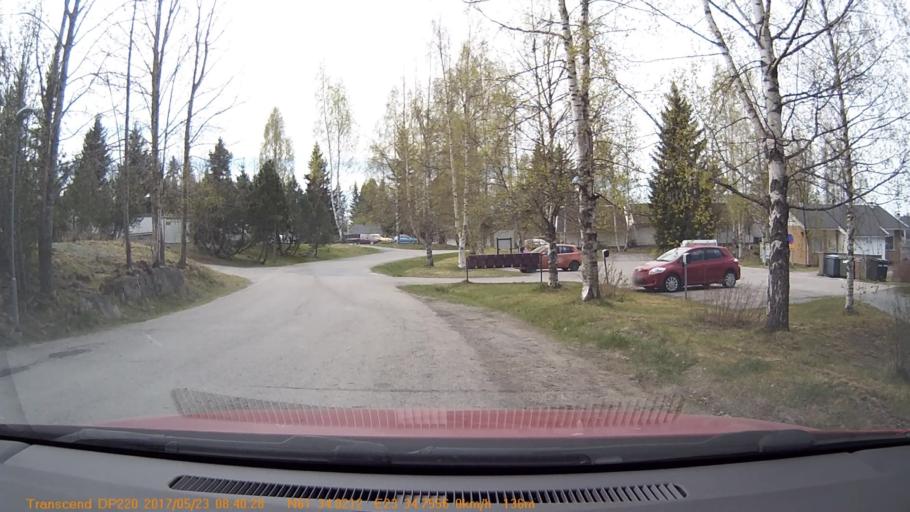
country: FI
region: Pirkanmaa
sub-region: Tampere
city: Yloejaervi
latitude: 61.5670
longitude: 23.5793
